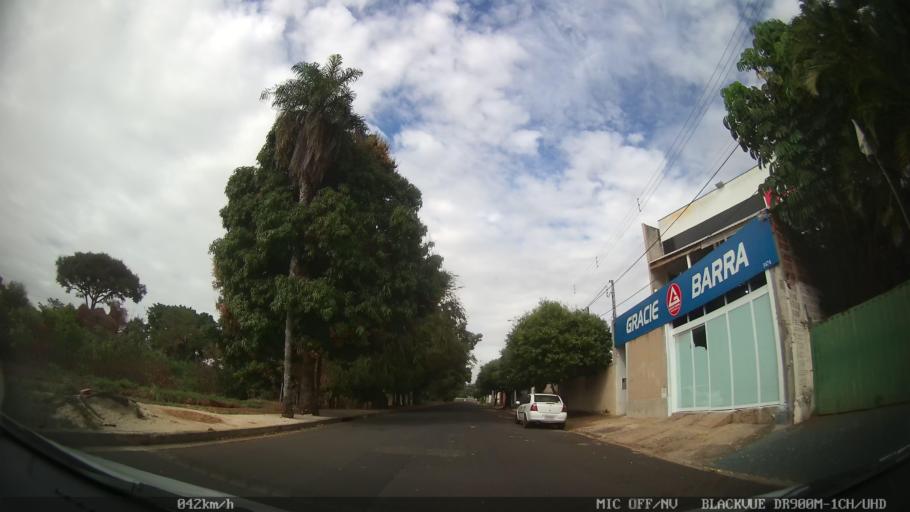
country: BR
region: Sao Paulo
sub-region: Sao Jose Do Rio Preto
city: Sao Jose do Rio Preto
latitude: -20.8232
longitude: -49.3488
